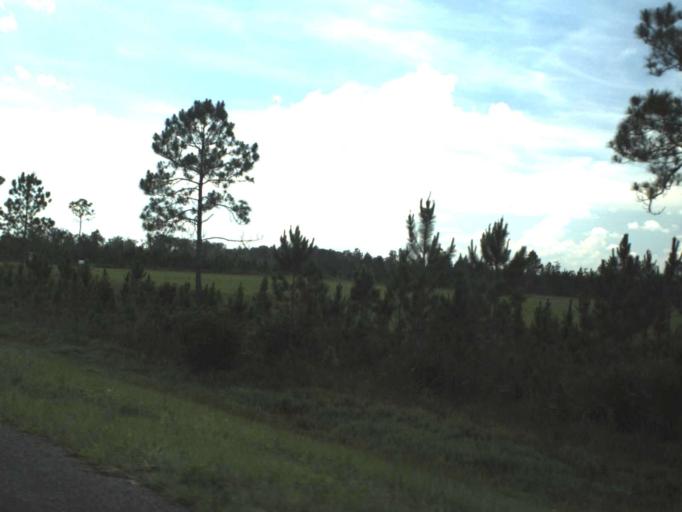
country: US
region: Florida
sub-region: Volusia County
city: Samsula-Spruce Creek
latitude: 29.0260
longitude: -81.1422
